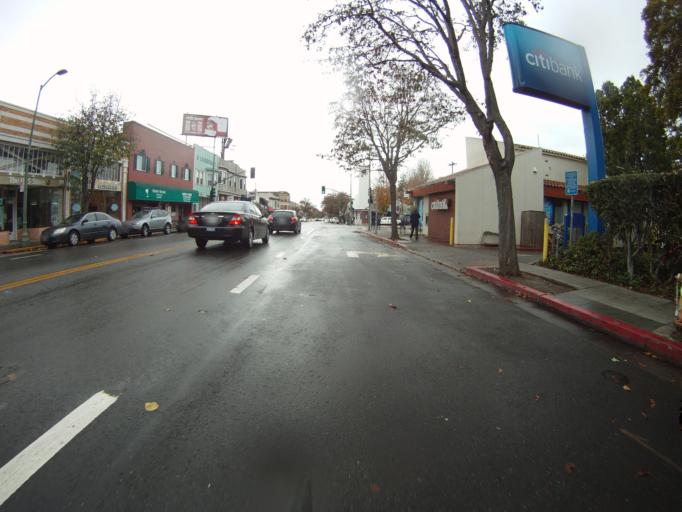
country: US
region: California
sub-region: Alameda County
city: Piedmont
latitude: 37.8266
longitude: -122.2523
